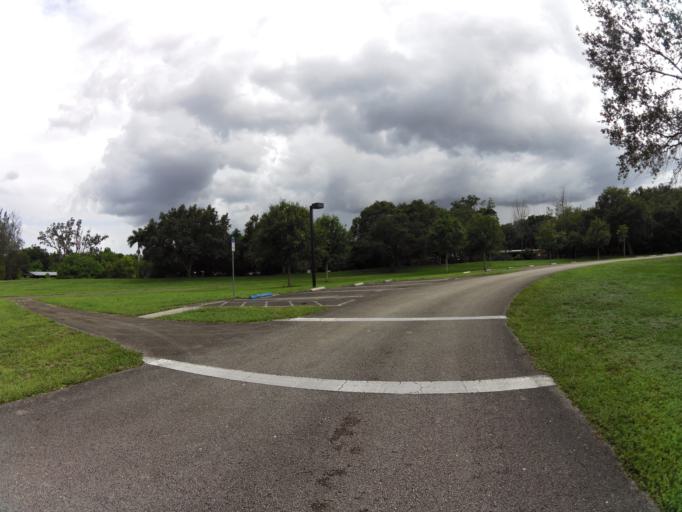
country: US
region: Florida
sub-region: Broward County
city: Cooper City
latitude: 26.0694
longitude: -80.2736
